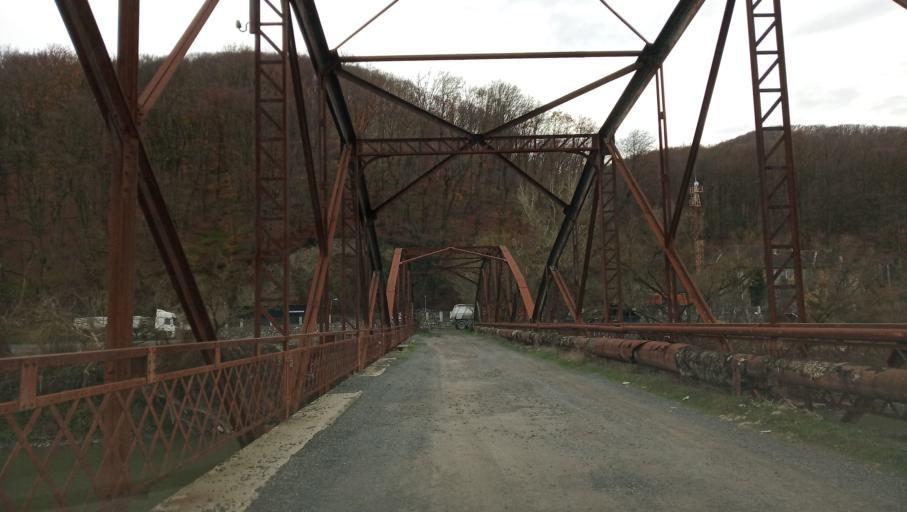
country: RO
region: Hunedoara
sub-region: Comuna Ilia
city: Ilia
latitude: 45.9221
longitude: 22.6634
